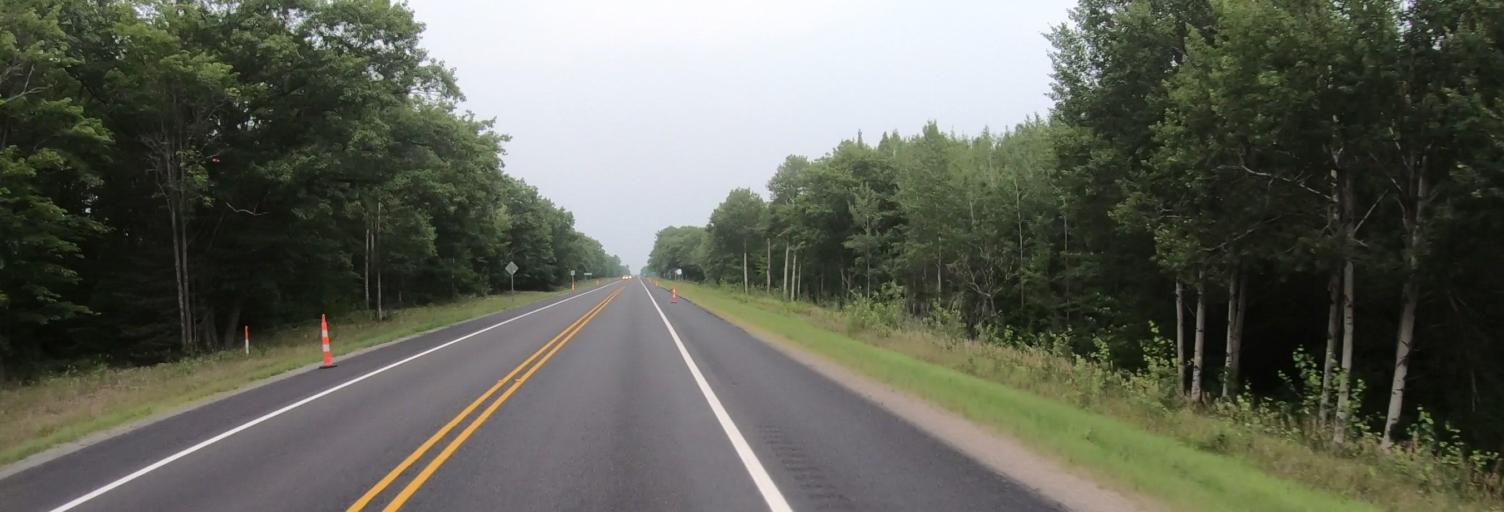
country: US
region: Michigan
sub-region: Mackinac County
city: Saint Ignace
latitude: 45.7037
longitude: -84.7695
